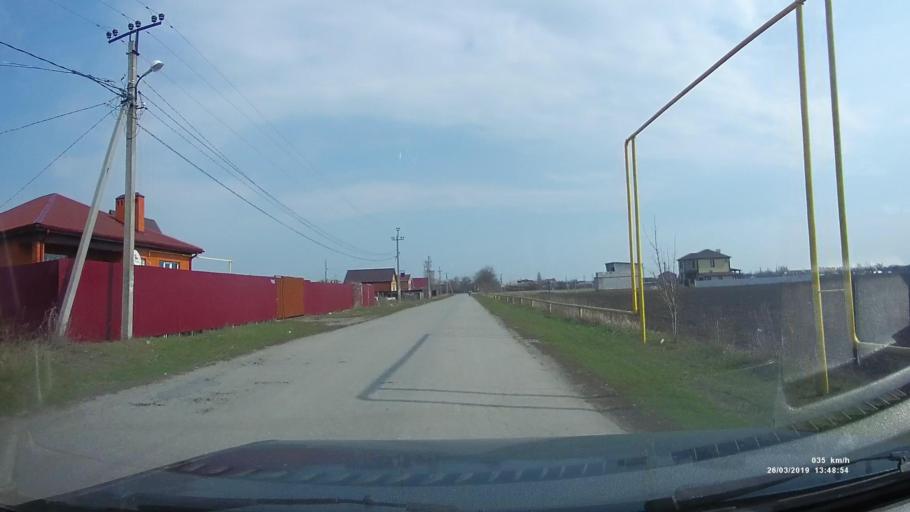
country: RU
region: Rostov
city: Novobessergenovka
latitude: 47.1915
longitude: 38.8620
